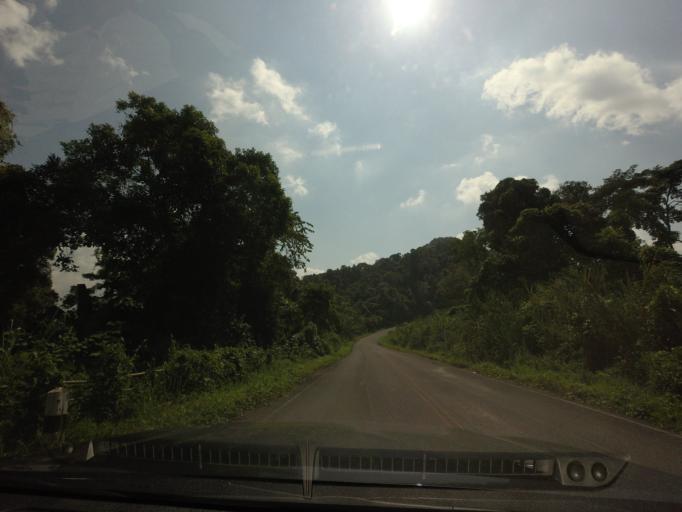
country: TH
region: Nan
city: Bo Kluea
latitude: 19.0680
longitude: 101.1222
